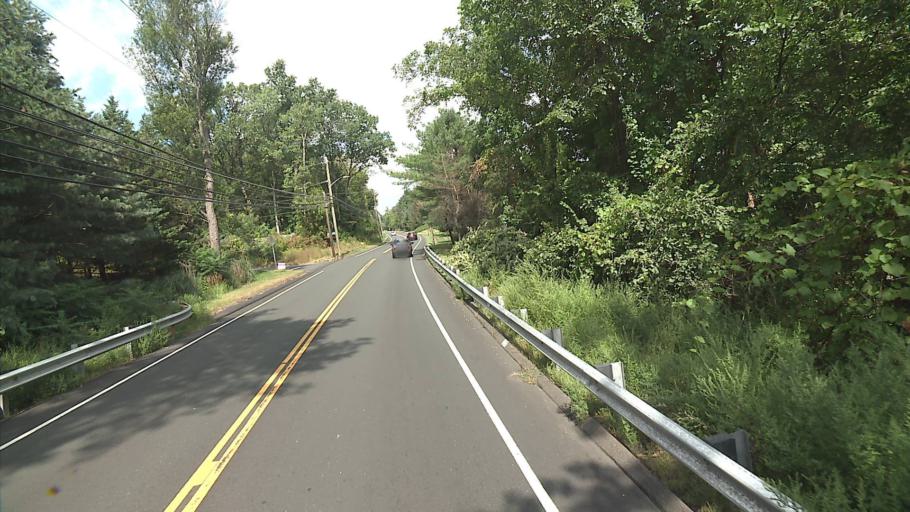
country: US
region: Connecticut
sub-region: Hartford County
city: Weatogue
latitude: 41.8314
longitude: -72.7739
